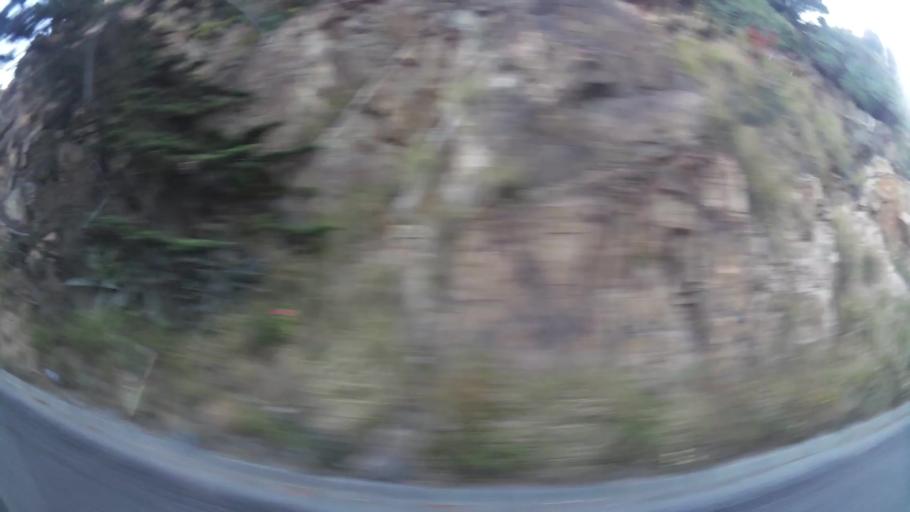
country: CL
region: Valparaiso
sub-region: Provincia de Valparaiso
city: Vina del Mar
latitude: -33.0264
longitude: -71.5820
